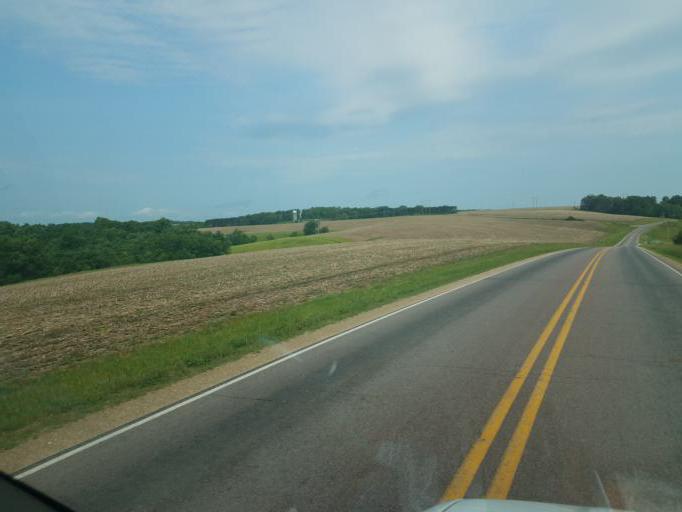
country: US
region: Wisconsin
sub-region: Vernon County
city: Hillsboro
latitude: 43.6529
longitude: -90.4555
